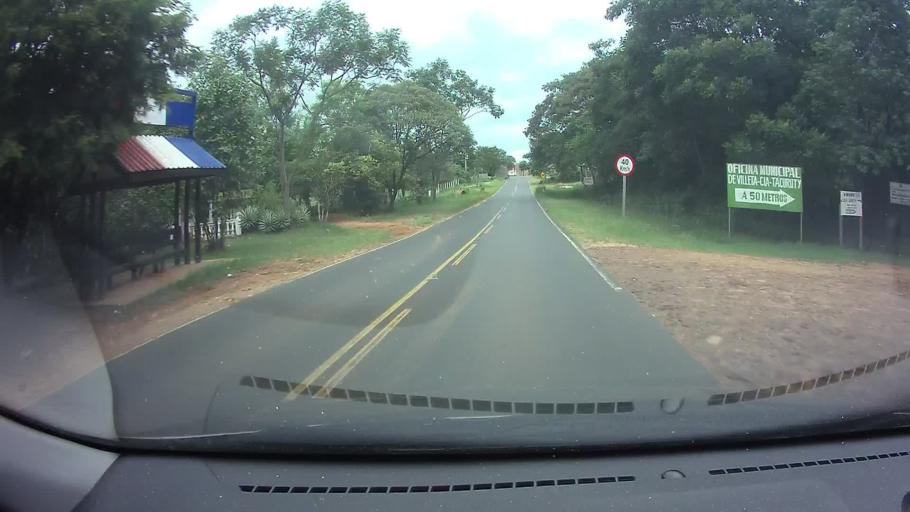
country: PY
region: Central
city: Guarambare
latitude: -25.5329
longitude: -57.4996
